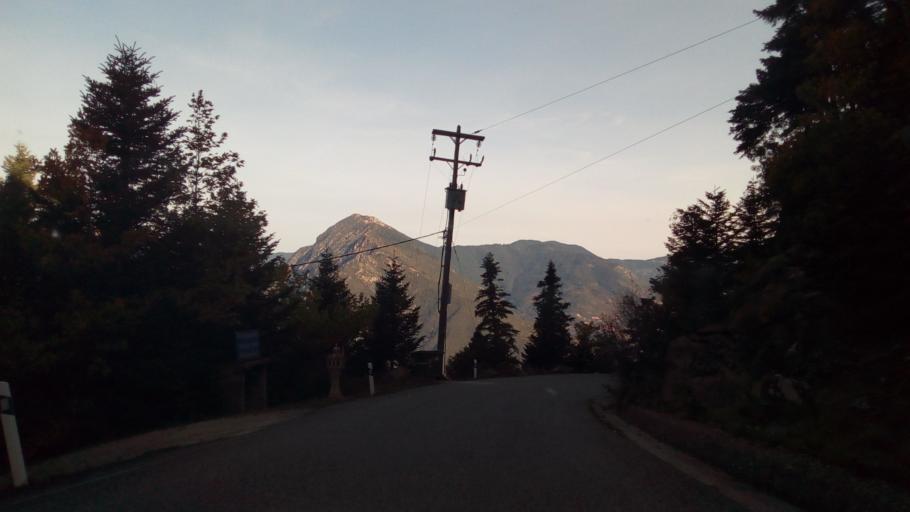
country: GR
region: West Greece
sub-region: Nomos Aitolias kai Akarnanias
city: Thermo
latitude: 38.6446
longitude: 21.8443
